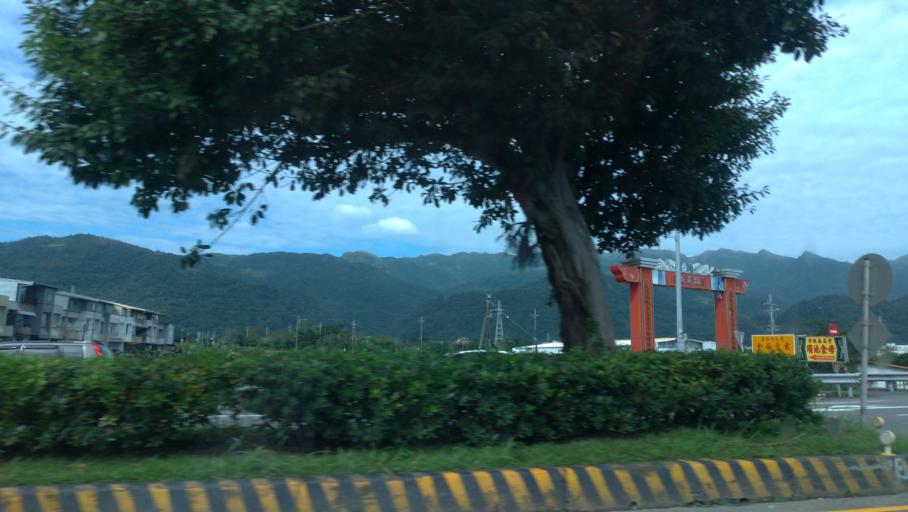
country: TW
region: Taiwan
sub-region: Yilan
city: Yilan
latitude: 24.8483
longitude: 121.8142
